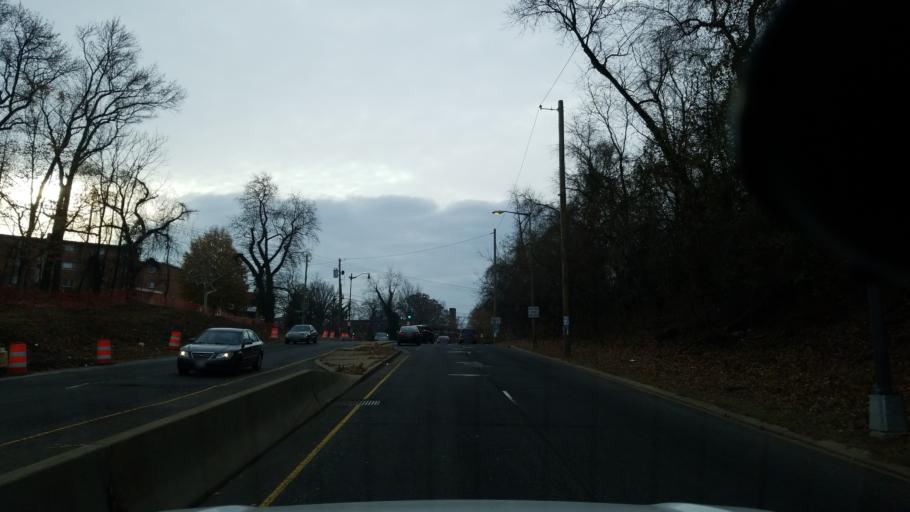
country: US
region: Maryland
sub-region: Prince George's County
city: Glassmanor
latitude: 38.8369
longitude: -77.0083
